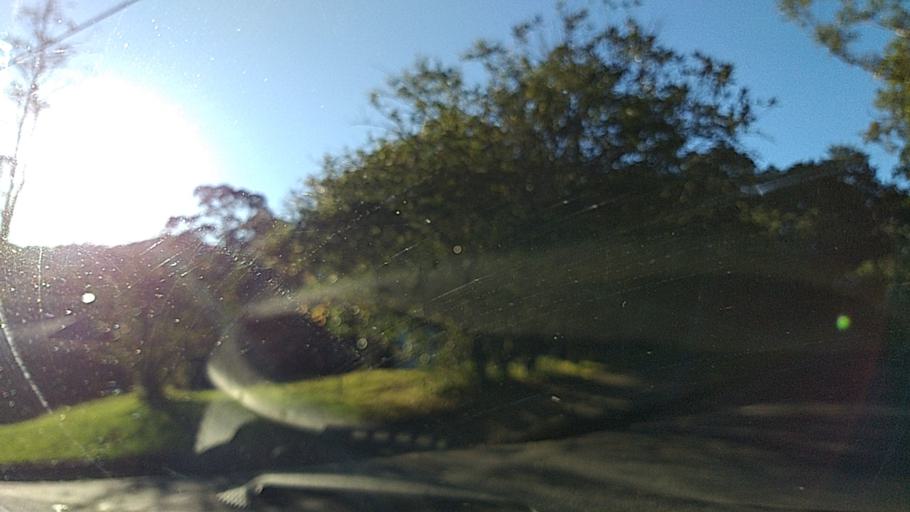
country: AU
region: New South Wales
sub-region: Wollongong
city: Mount Keira
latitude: -34.4306
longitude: 150.8535
